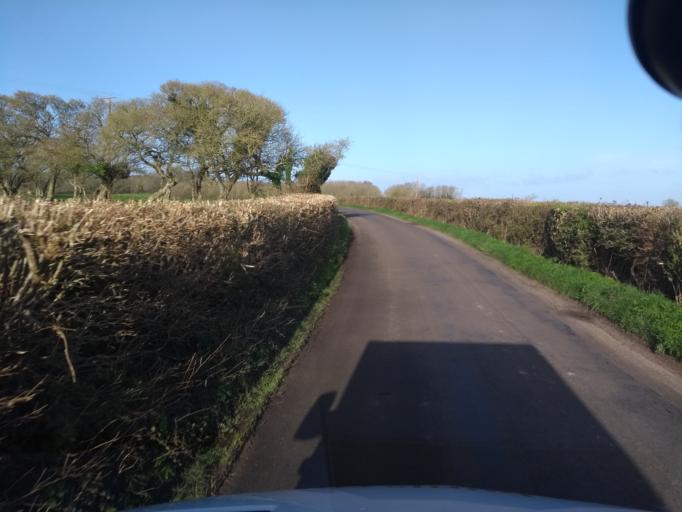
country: GB
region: England
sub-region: Somerset
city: Westonzoyland
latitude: 51.1367
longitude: -2.8426
